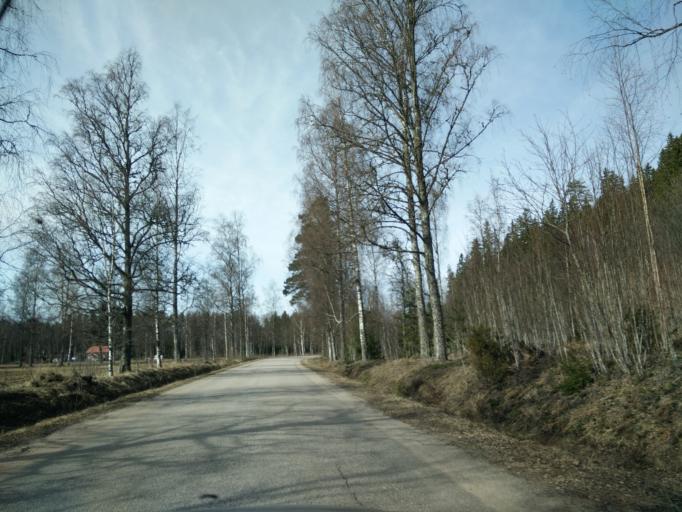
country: SE
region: Vaermland
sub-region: Hagfors Kommun
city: Hagfors
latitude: 60.0386
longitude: 13.6003
